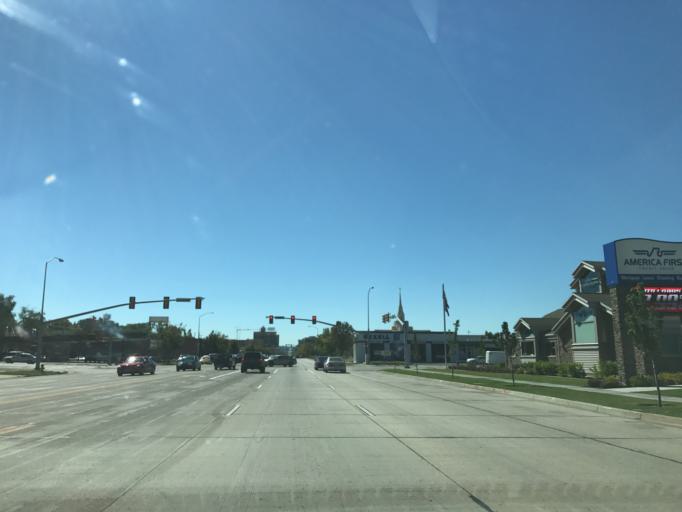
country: US
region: Utah
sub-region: Weber County
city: Ogden
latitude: 41.2318
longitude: -111.9703
